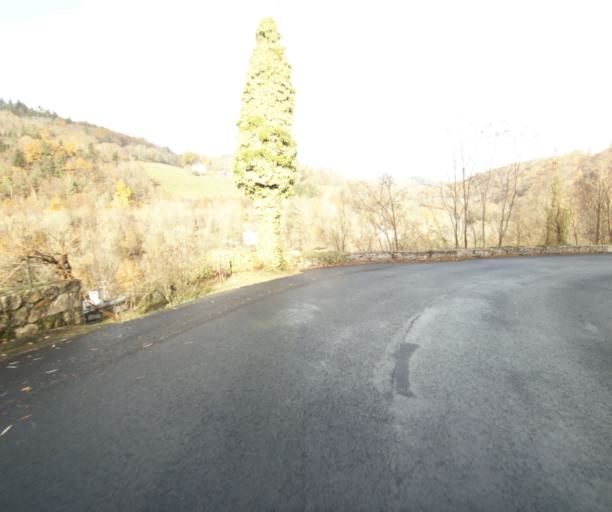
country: FR
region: Limousin
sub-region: Departement de la Correze
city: Cornil
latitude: 45.2146
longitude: 1.6975
